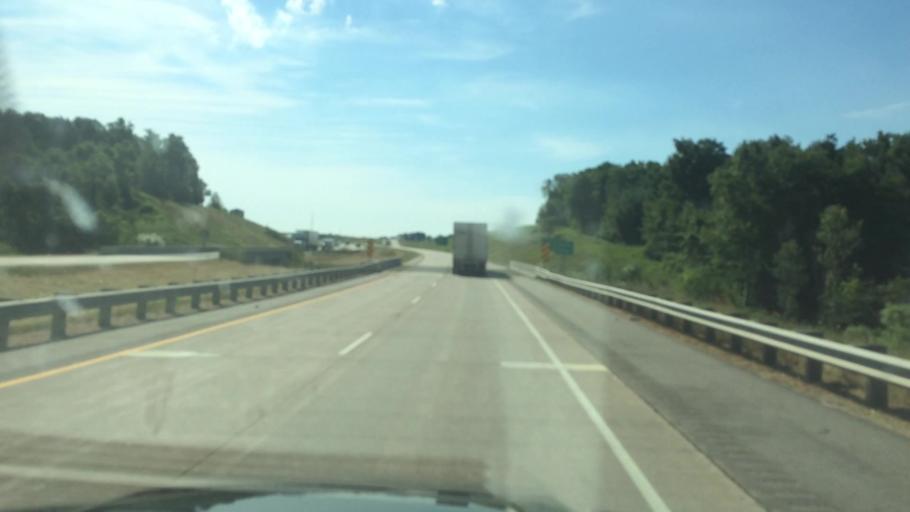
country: US
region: Wisconsin
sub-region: Shawano County
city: Bonduel
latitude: 44.7309
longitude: -88.4567
